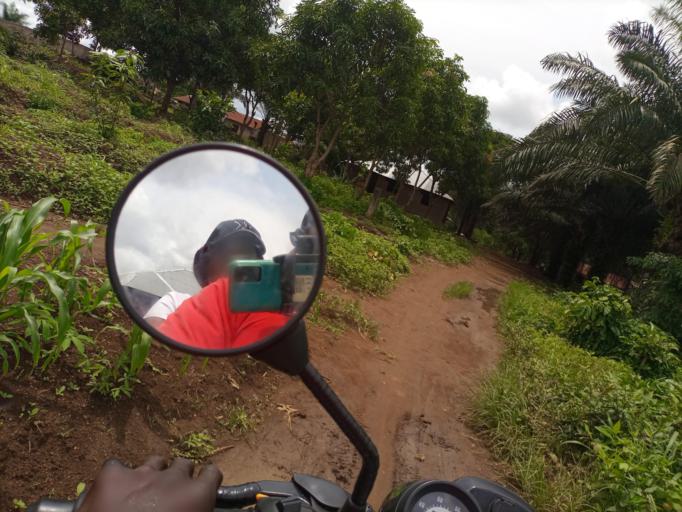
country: SL
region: Southern Province
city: Baoma
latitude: 7.9731
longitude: -11.7112
